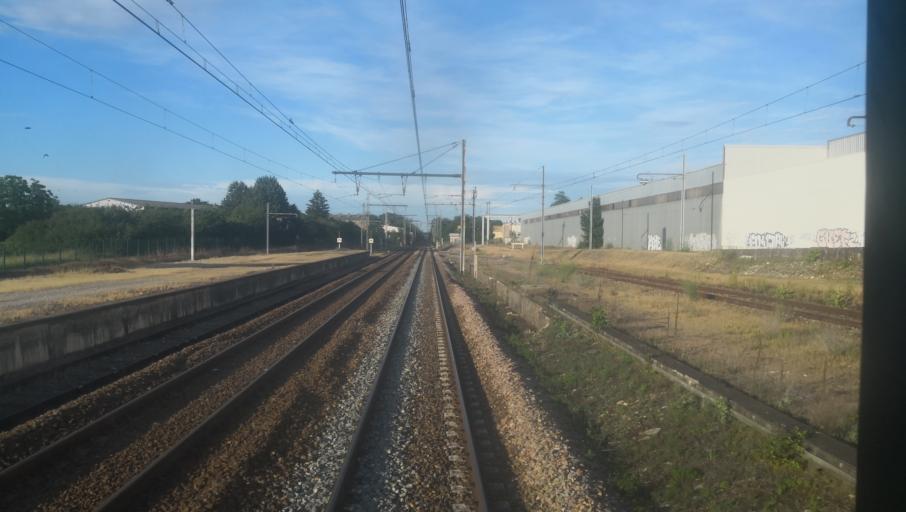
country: FR
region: Centre
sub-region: Departement de l'Indre
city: Deols
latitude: 46.8176
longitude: 1.7193
